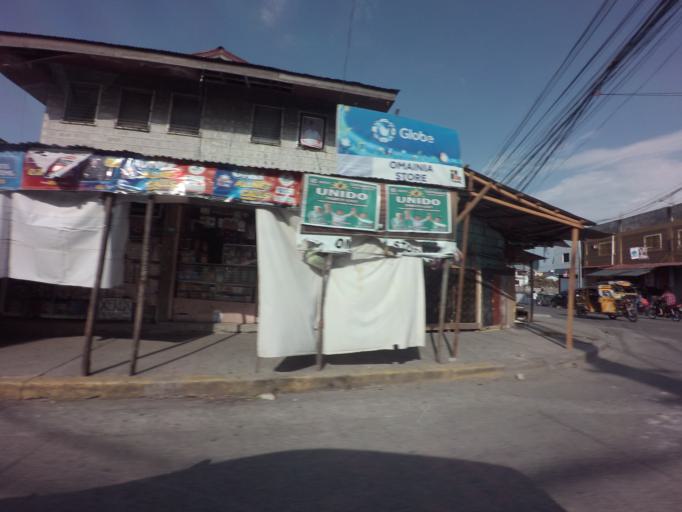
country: PH
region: Calabarzon
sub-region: Province of Rizal
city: Taguig
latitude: 14.4974
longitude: 121.0556
